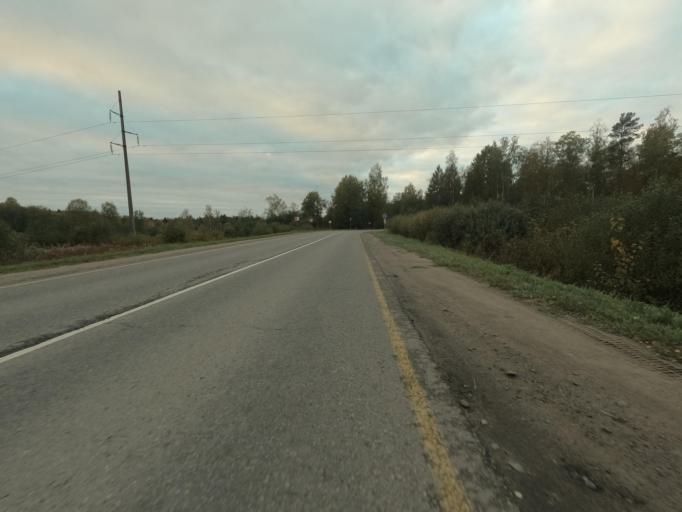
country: RU
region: Leningrad
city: Pavlovo
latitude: 59.8023
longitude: 30.9380
